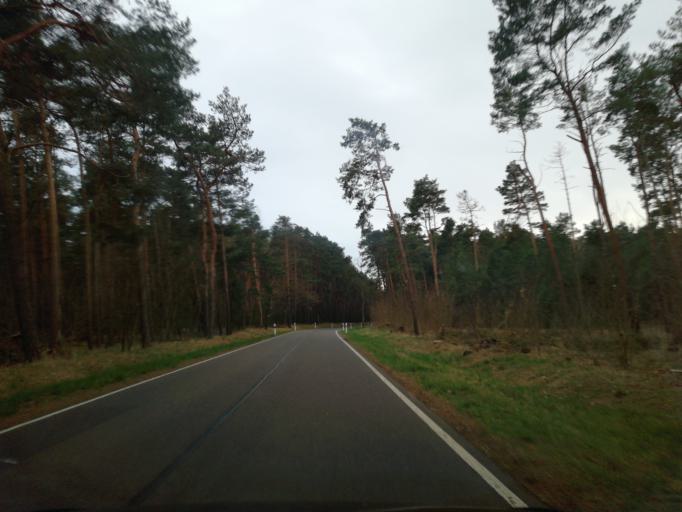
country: DE
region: Brandenburg
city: Vetschau
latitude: 51.7350
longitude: 14.1278
